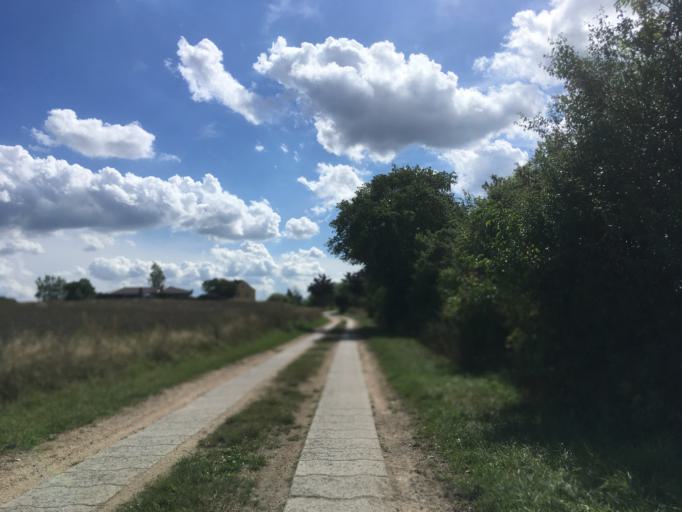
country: DE
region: Brandenburg
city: Gerswalde
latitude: 53.0963
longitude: 13.8694
